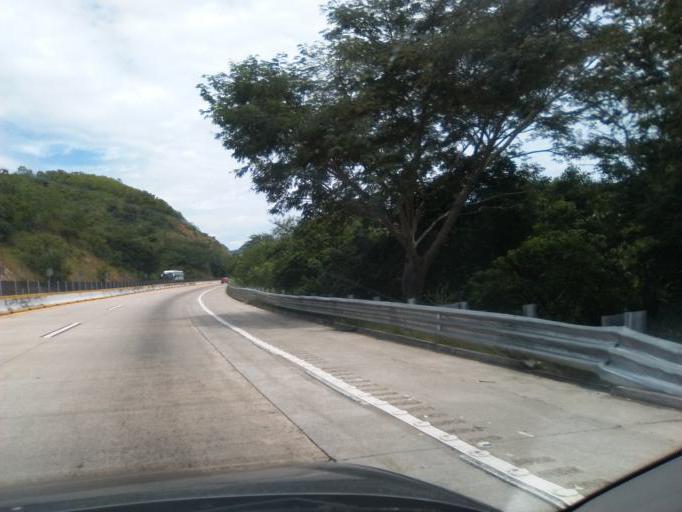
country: MX
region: Guerrero
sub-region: Chilpancingo de los Bravo
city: Julian Blanco (Dos Caminos)
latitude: 17.2116
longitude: -99.5362
